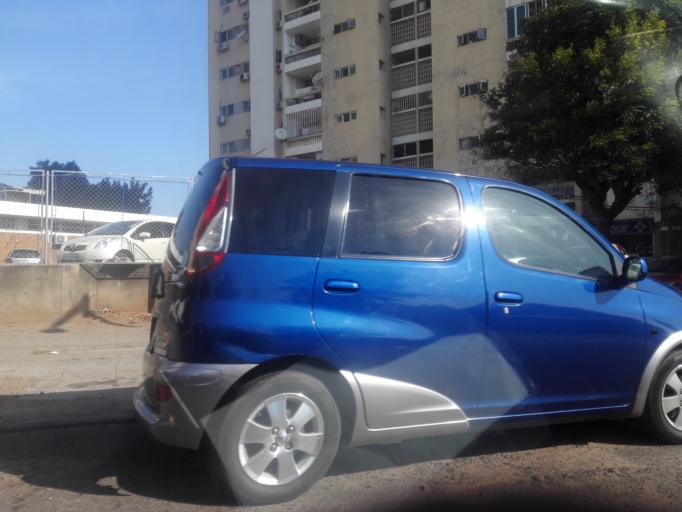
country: MZ
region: Maputo City
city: Maputo
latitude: -25.9552
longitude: 32.5871
